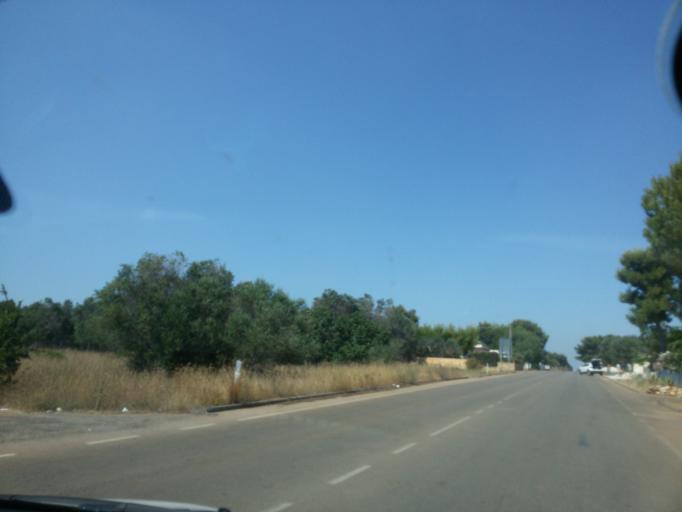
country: IT
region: Apulia
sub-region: Provincia di Lecce
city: Porto Cesareo
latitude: 40.2256
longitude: 17.9416
